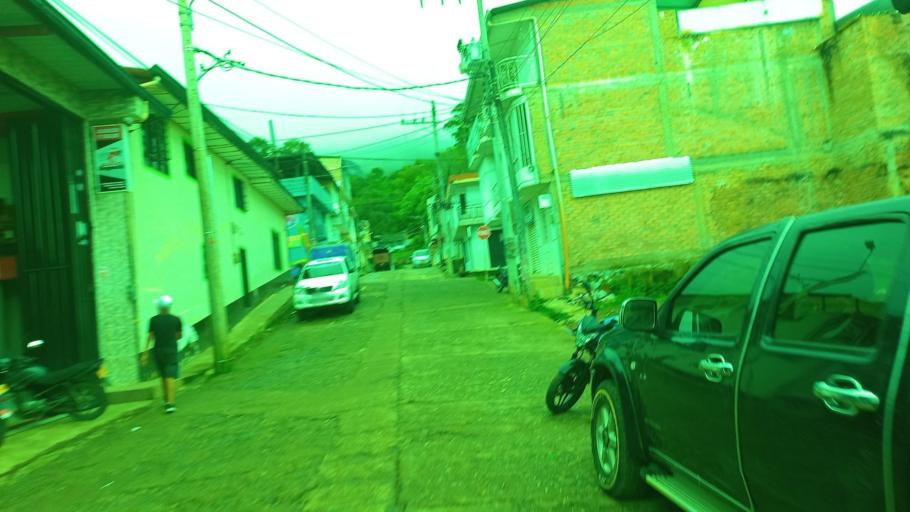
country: CO
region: Cauca
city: Balboa
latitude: 2.0414
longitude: -77.2157
